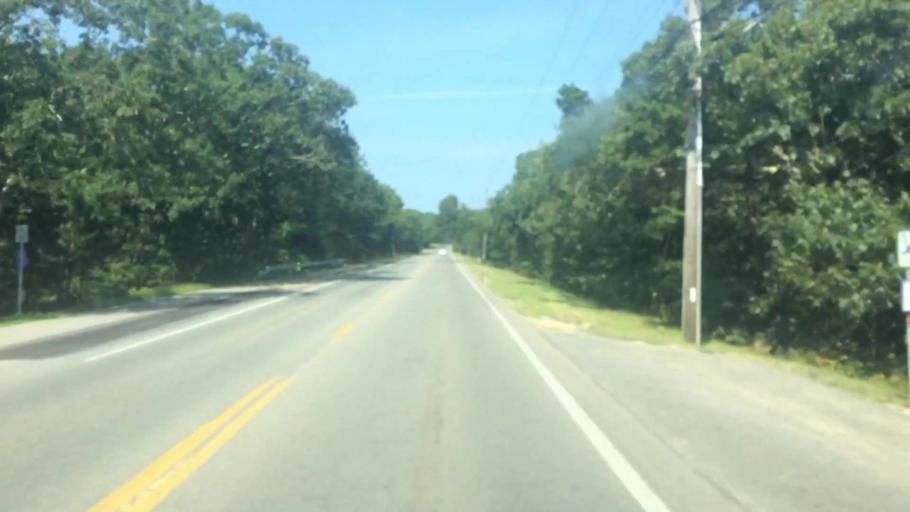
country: US
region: Massachusetts
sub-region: Dukes County
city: Oak Bluffs
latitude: 41.4081
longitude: -70.5671
